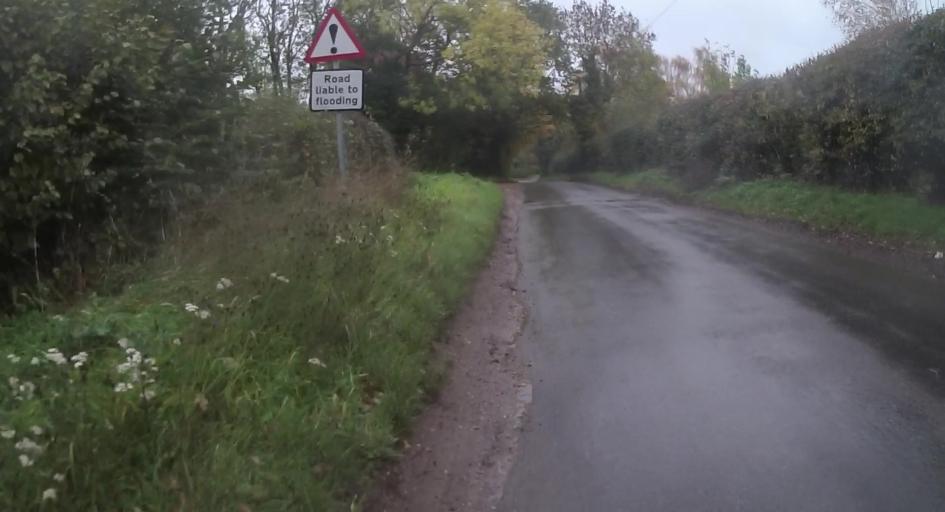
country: GB
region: England
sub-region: Surrey
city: Farnham
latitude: 51.2146
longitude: -0.8483
